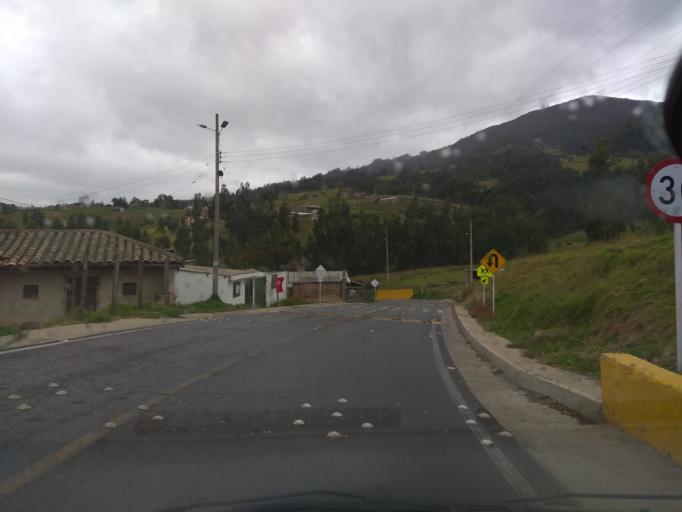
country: CO
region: Boyaca
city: Topaga
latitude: 5.7495
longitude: -72.8456
